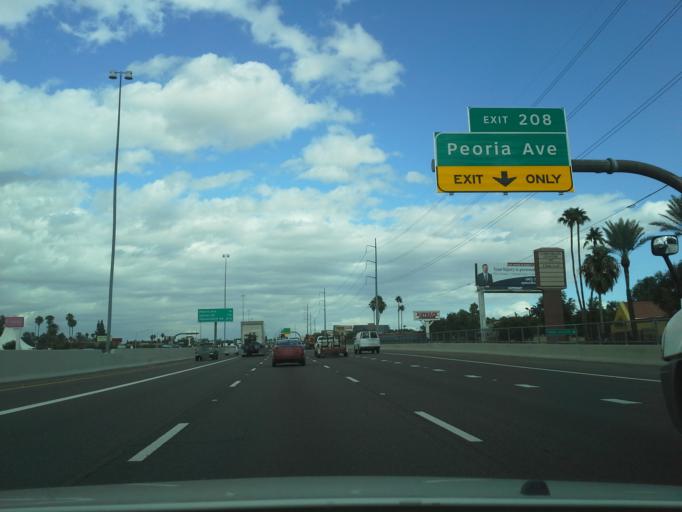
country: US
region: Arizona
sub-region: Maricopa County
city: Glendale
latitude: 33.5735
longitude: -112.1170
